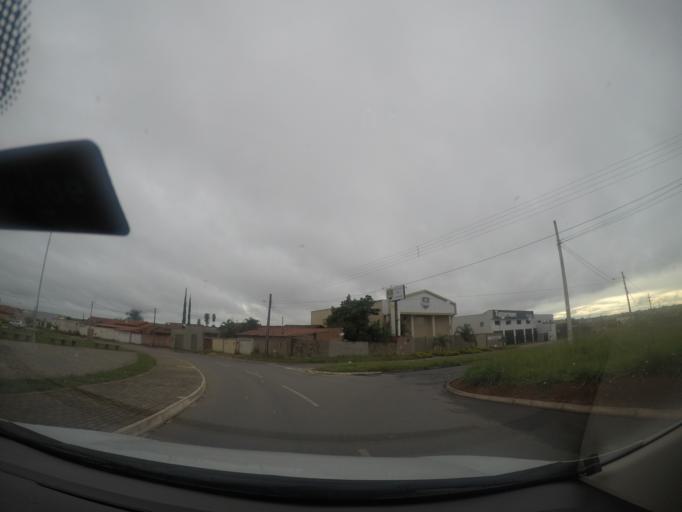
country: BR
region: Goias
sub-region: Goiania
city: Goiania
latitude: -16.7537
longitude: -49.3202
